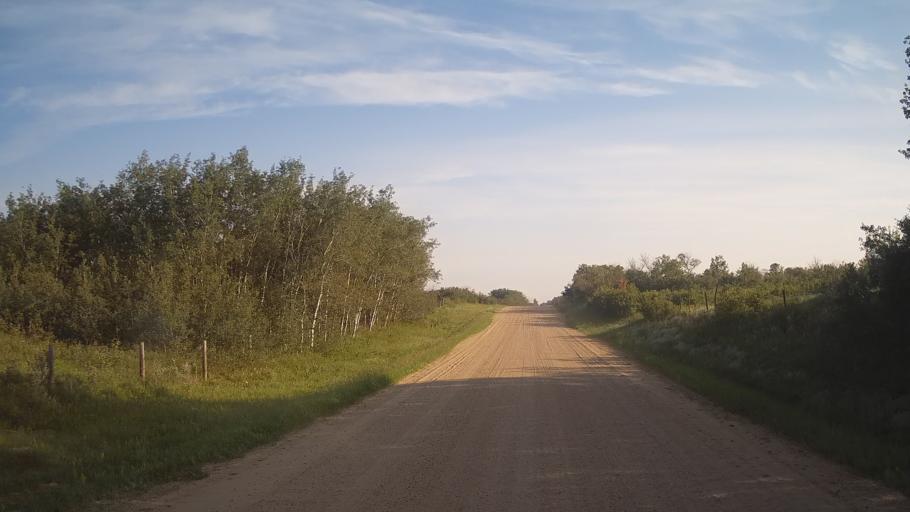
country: CA
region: Saskatchewan
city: Saskatoon
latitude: 51.8386
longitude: -106.5240
